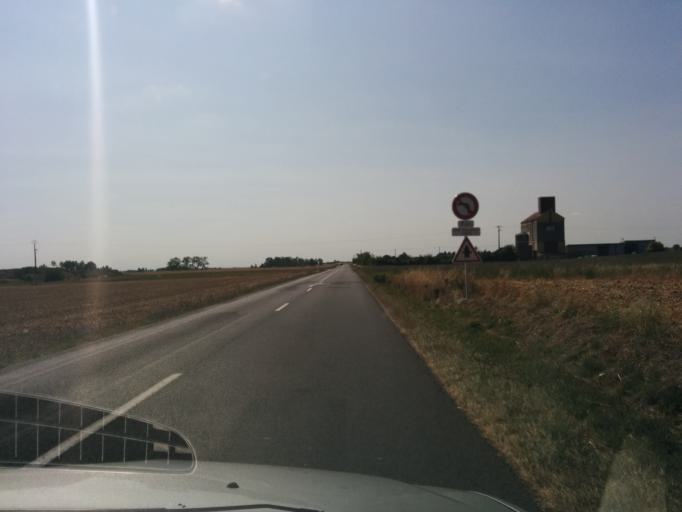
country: FR
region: Poitou-Charentes
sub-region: Departement de la Vienne
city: Saint-Jean-de-Sauves
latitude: 46.8005
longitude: 0.0919
